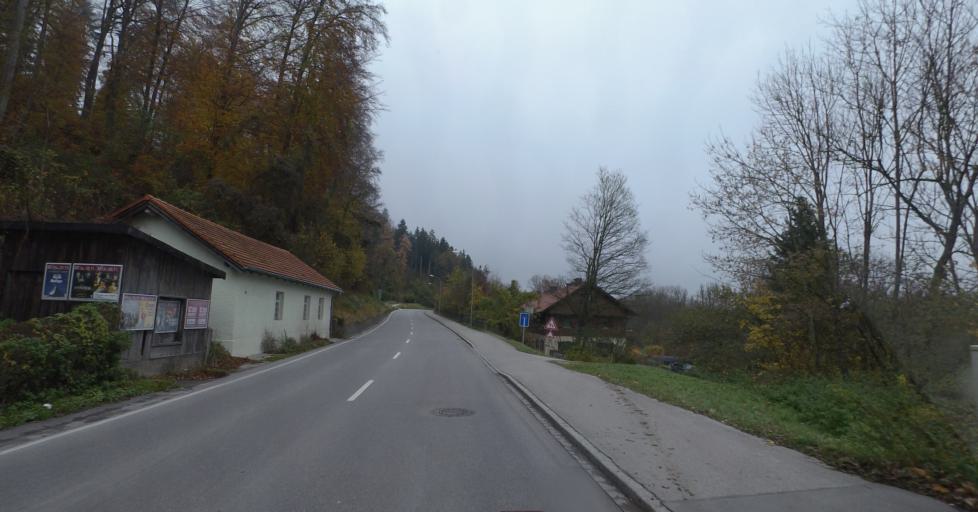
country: DE
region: Bavaria
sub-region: Upper Bavaria
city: Trostberg an der Alz
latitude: 48.0358
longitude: 12.5604
